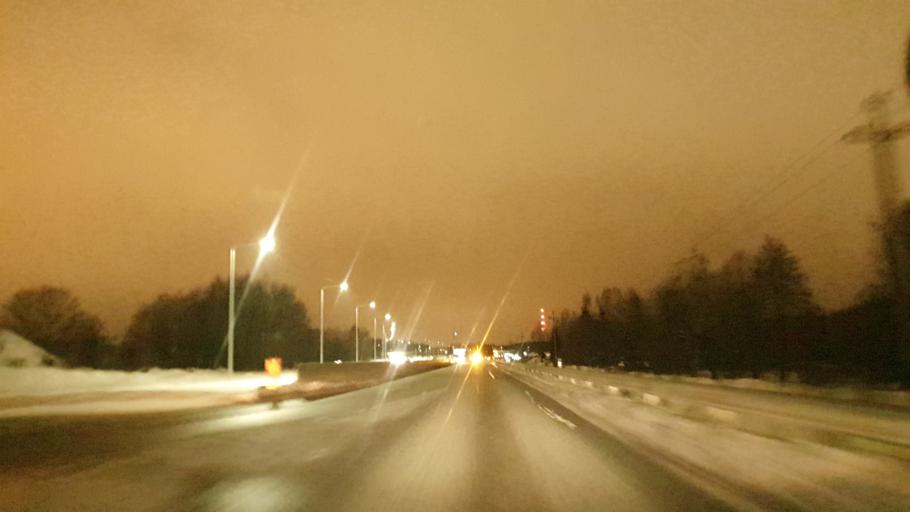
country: EE
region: Harju
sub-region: Joelaehtme vald
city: Loo
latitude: 59.4378
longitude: 24.9141
